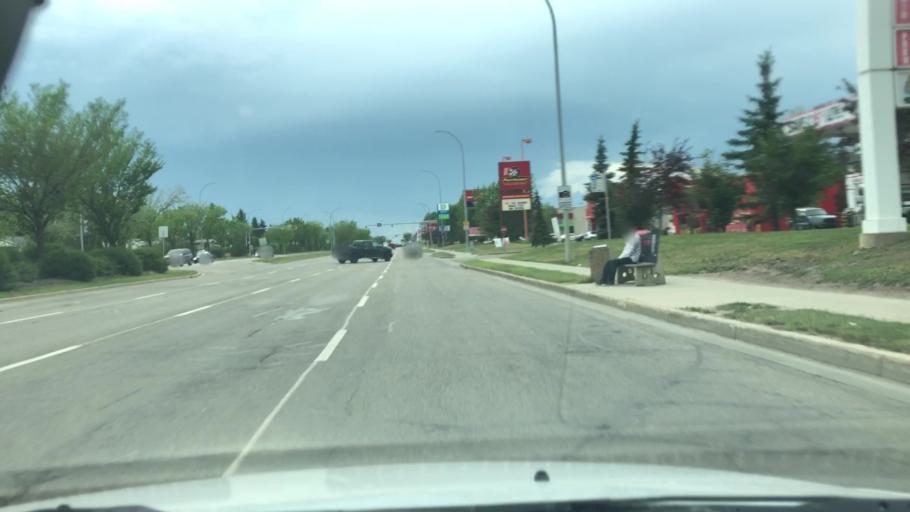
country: CA
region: Alberta
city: Edmonton
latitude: 53.5996
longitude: -113.5442
